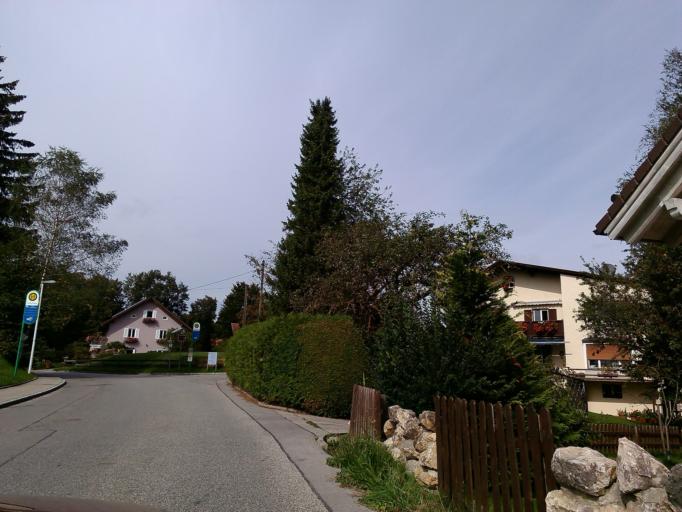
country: DE
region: Bavaria
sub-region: Upper Bavaria
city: Pocking
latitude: 47.9864
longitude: 11.2956
